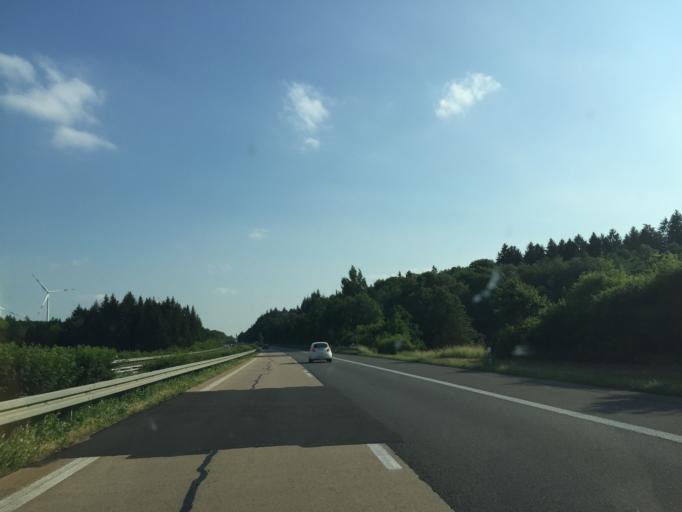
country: DE
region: Baden-Wuerttemberg
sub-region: Regierungsbezirk Stuttgart
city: Buch am Ahorn
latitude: 49.5265
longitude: 9.5736
